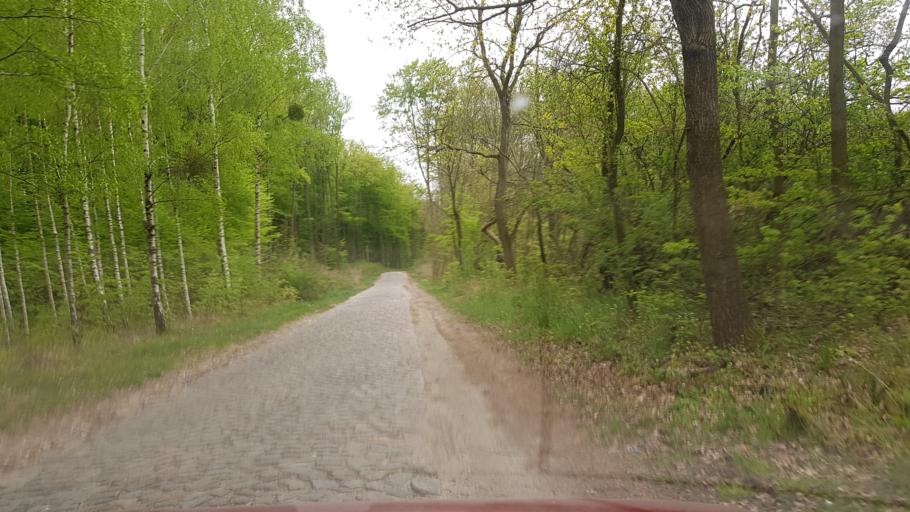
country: PL
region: West Pomeranian Voivodeship
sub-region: Powiat gryfinski
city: Stare Czarnowo
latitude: 53.2943
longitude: 14.7258
